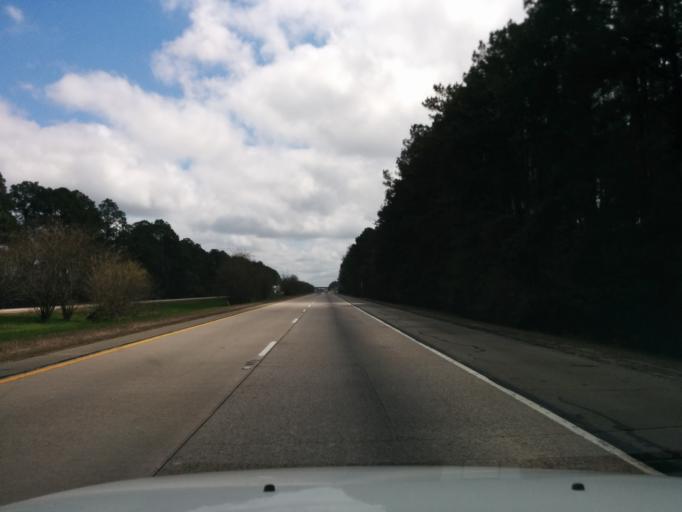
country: US
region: Georgia
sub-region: Bryan County
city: Pembroke
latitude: 32.1872
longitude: -81.4683
